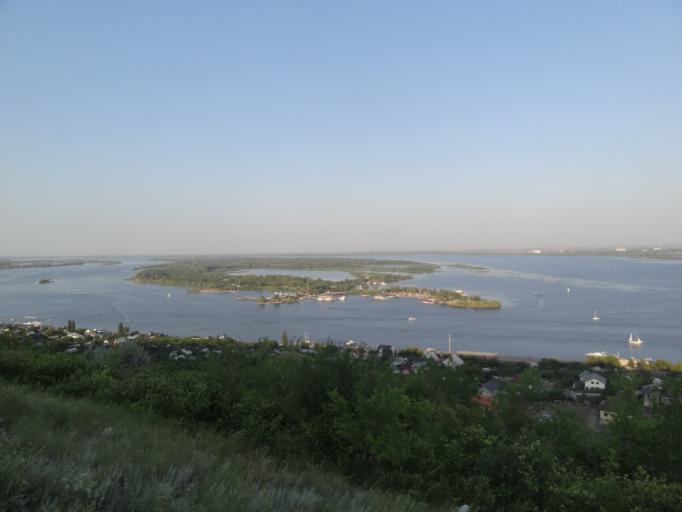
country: RU
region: Saratov
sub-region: Saratovskiy Rayon
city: Saratov
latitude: 51.5367
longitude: 46.0698
